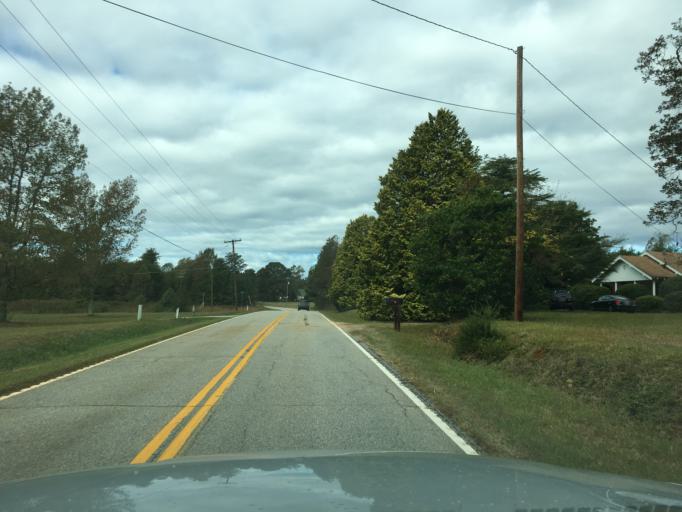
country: US
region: South Carolina
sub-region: Greenville County
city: Tigerville
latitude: 35.0605
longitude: -82.2686
